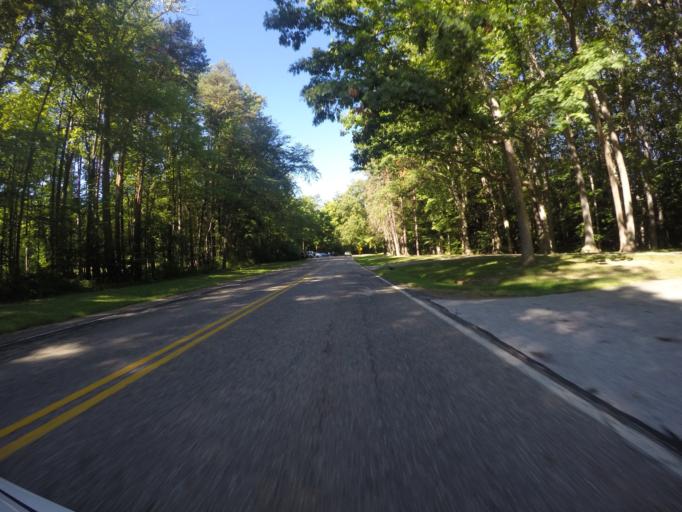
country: US
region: Ohio
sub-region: Cuyahoga County
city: Brecksville
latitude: 41.3188
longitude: -81.6181
